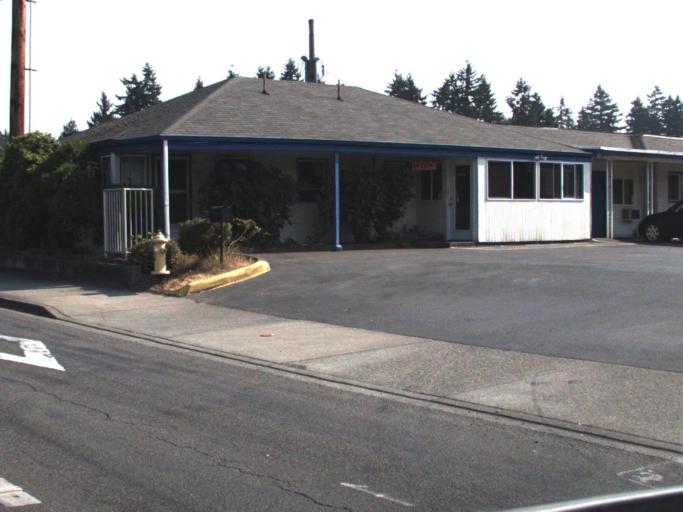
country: US
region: Washington
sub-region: King County
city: Federal Way
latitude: 47.3017
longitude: -122.3133
